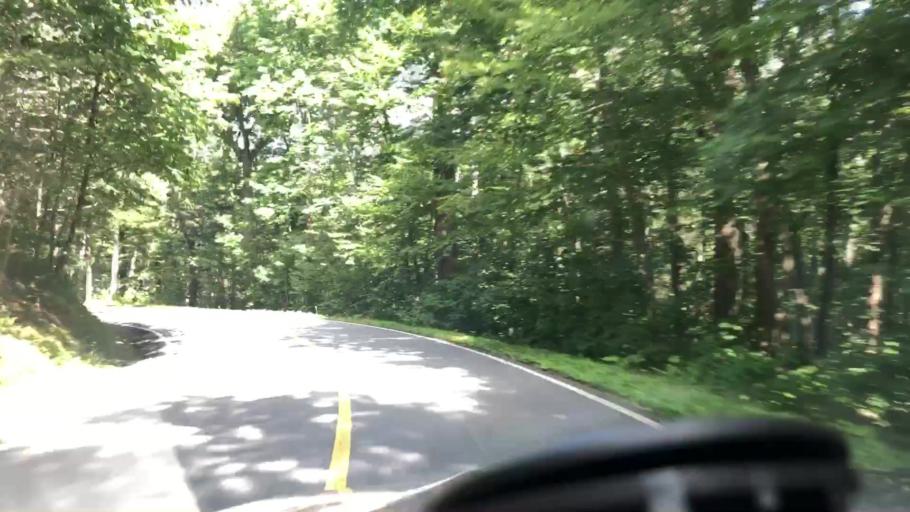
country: US
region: Massachusetts
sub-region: Berkshire County
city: Lanesborough
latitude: 42.5954
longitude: -73.1996
